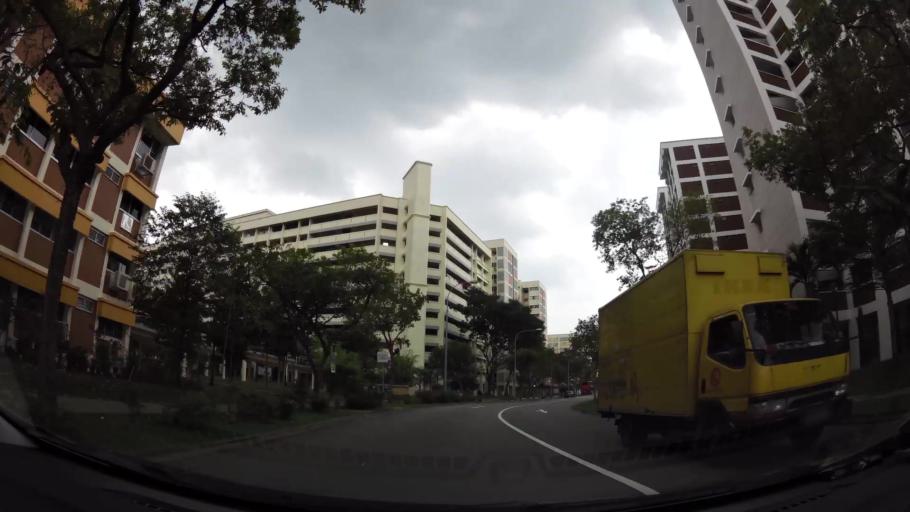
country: SG
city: Singapore
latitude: 1.3544
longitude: 103.9347
